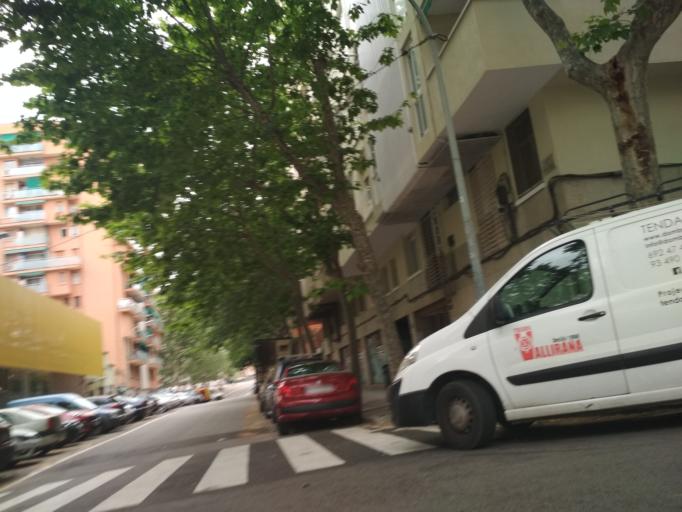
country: ES
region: Catalonia
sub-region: Provincia de Barcelona
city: Sant Marti
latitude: 41.4188
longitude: 2.2049
